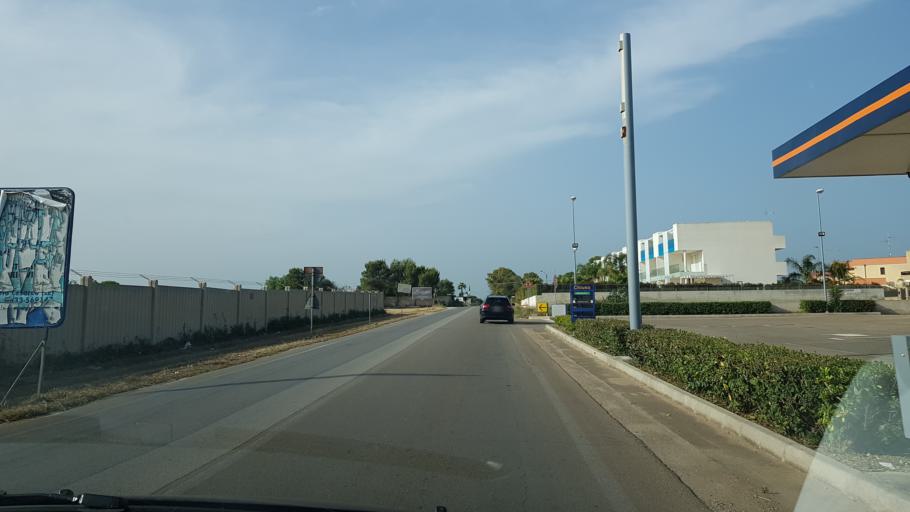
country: IT
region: Apulia
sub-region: Provincia di Lecce
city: Porto Cesareo
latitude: 40.2966
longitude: 17.8561
